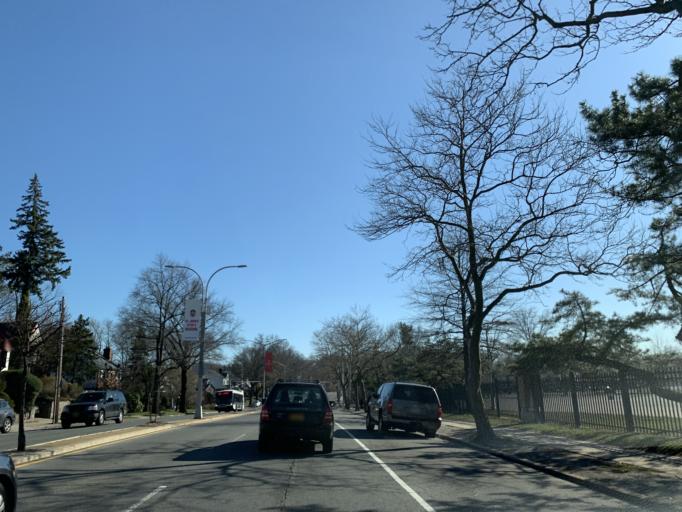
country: US
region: New York
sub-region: Queens County
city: Jamaica
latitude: 40.7225
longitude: -73.7904
